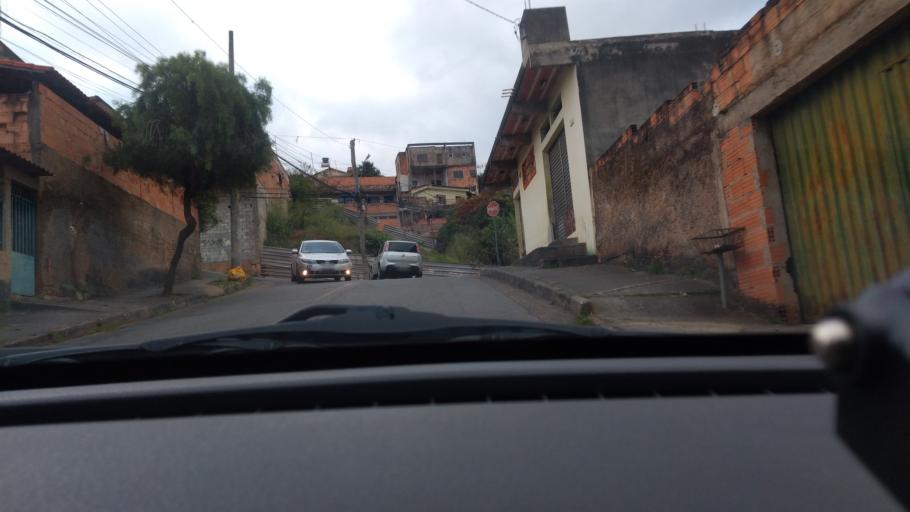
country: BR
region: Minas Gerais
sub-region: Santa Luzia
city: Santa Luzia
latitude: -19.8154
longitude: -43.9374
